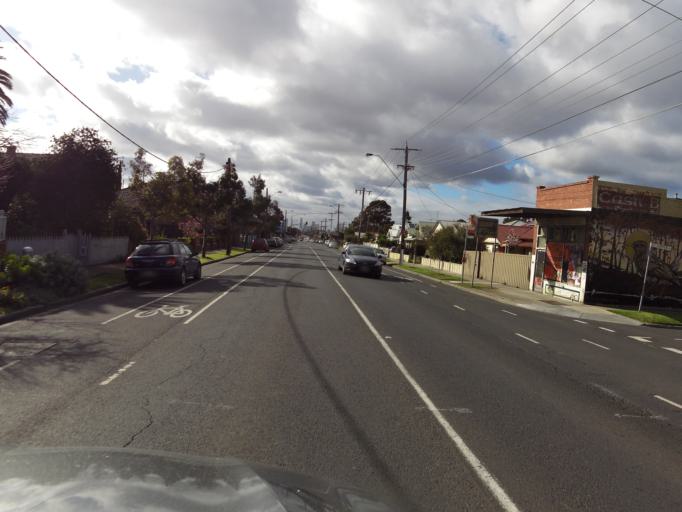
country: AU
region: Victoria
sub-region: Maribyrnong
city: Kingsville
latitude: -37.8122
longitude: 144.8780
